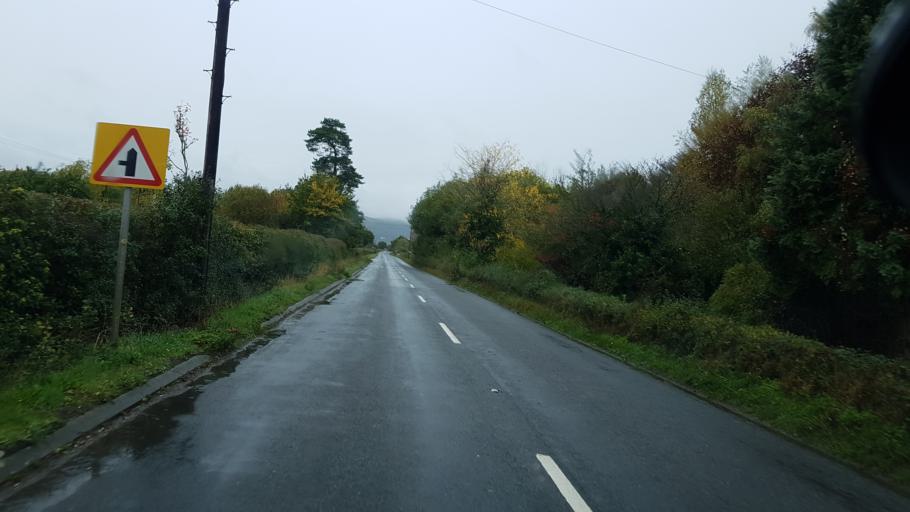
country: GB
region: England
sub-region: Worcestershire
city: Upton upon Severn
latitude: 52.0576
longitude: -2.2643
